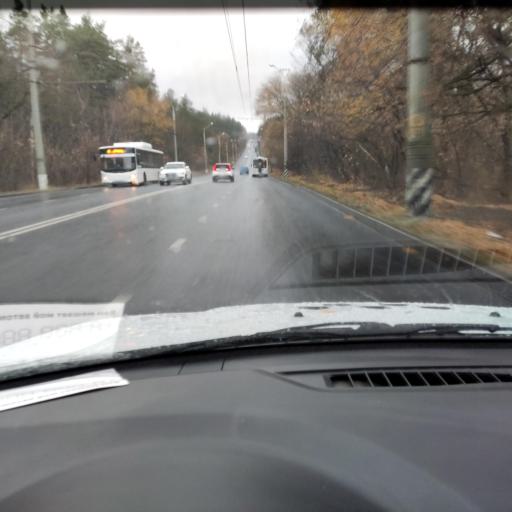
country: RU
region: Samara
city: Zhigulevsk
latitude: 53.5022
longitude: 49.4634
